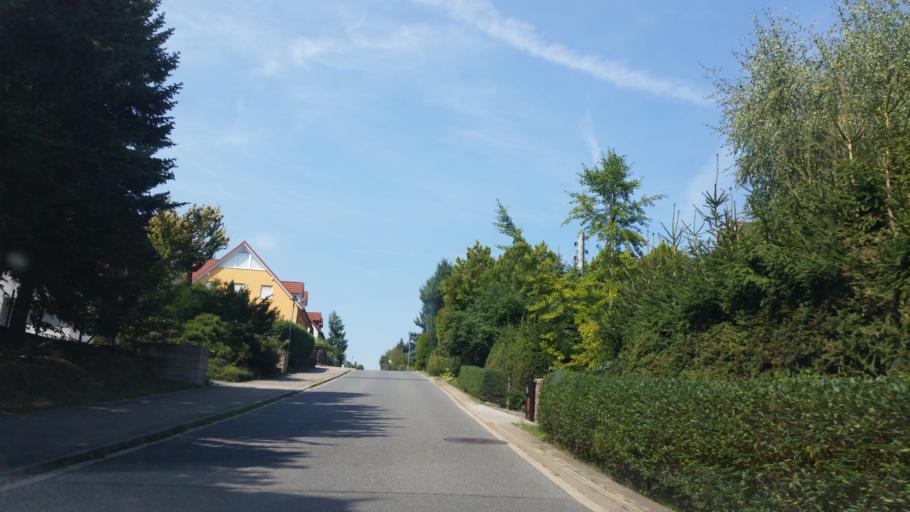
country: DE
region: Saxony
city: Klipphausen
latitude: 51.0712
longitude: 13.5302
